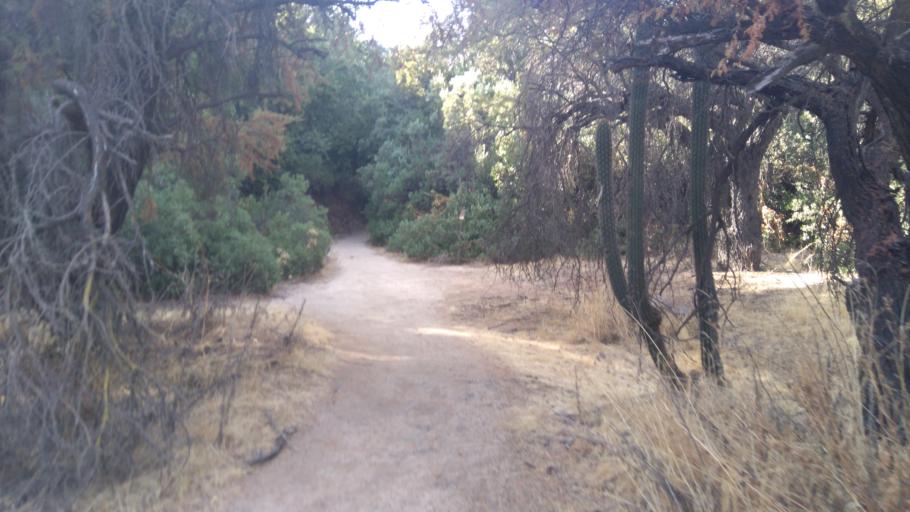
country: CL
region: Santiago Metropolitan
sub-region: Provincia de Cordillera
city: Puente Alto
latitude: -33.7256
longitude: -70.4776
